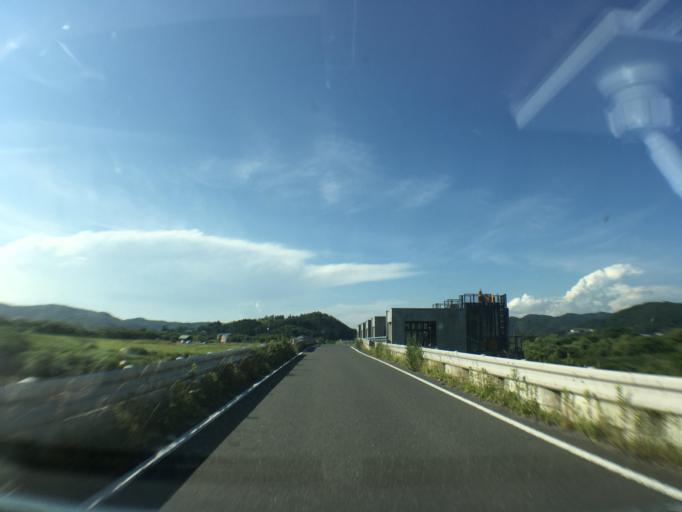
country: JP
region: Miyagi
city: Wakuya
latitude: 38.6012
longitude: 141.2926
